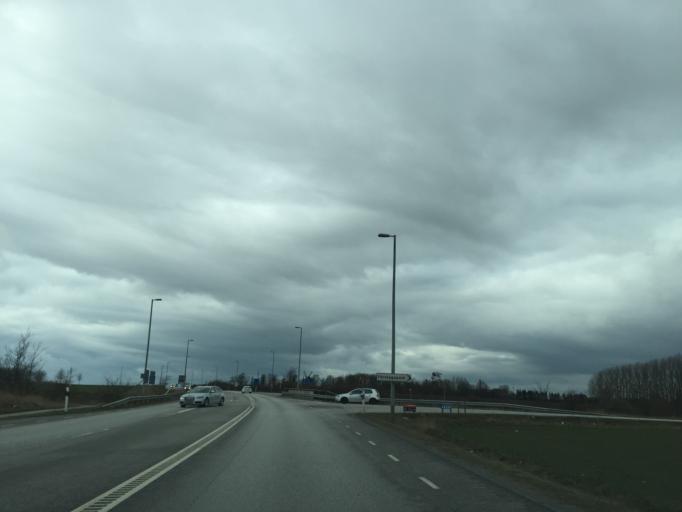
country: SE
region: Skane
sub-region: Lunds Kommun
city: Lund
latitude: 55.6804
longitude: 13.1769
